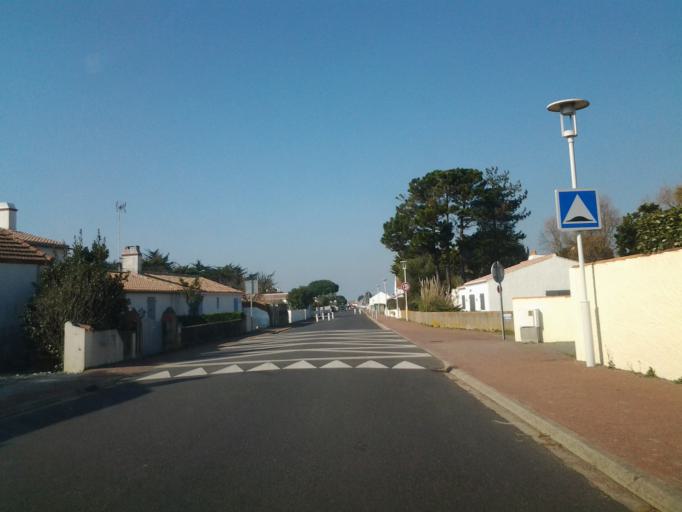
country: FR
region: Pays de la Loire
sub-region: Departement de la Vendee
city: La Gueriniere
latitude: 46.9672
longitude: -2.2196
